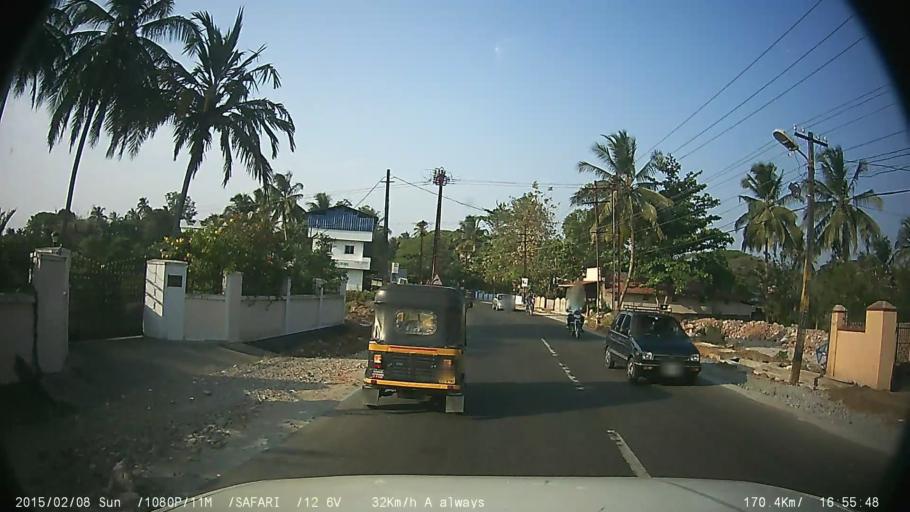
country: IN
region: Kerala
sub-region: Palakkad district
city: Palakkad
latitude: 10.7578
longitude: 76.6522
